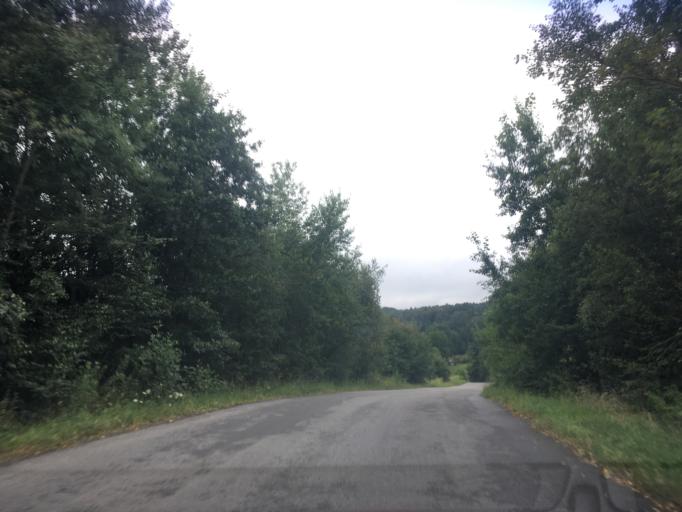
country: PL
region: Lesser Poland Voivodeship
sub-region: Powiat myslenicki
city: Brzaczowice
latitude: 49.8554
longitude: 20.0208
